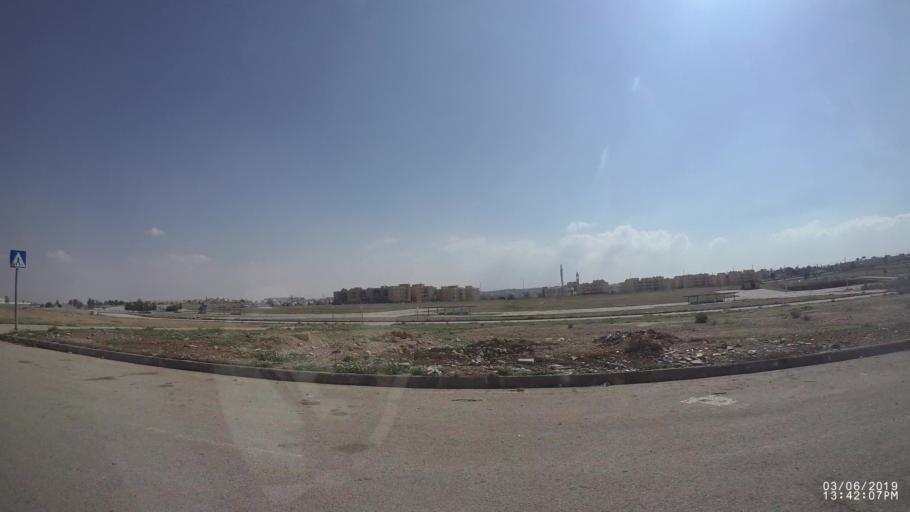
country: JO
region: Zarqa
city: Zarqa
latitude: 32.0709
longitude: 36.1092
